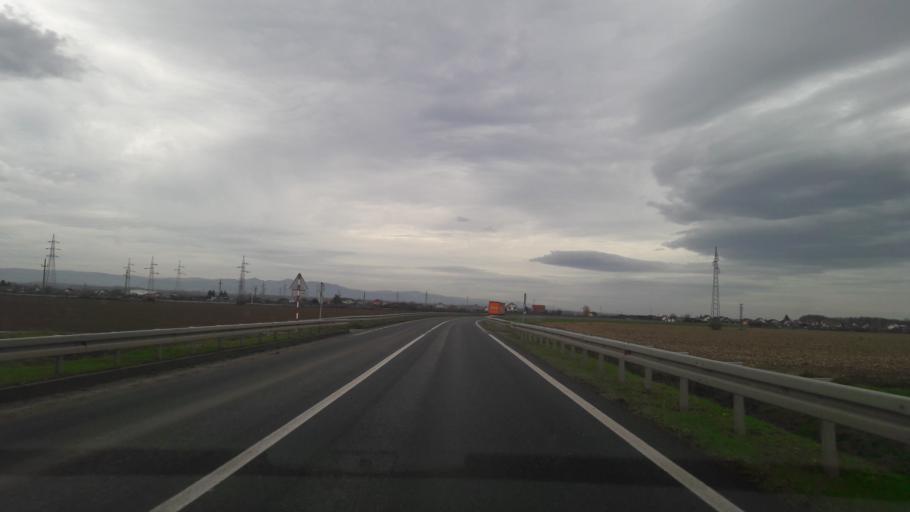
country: HR
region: Osjecko-Baranjska
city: Velimirovac
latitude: 45.5106
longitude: 18.1064
